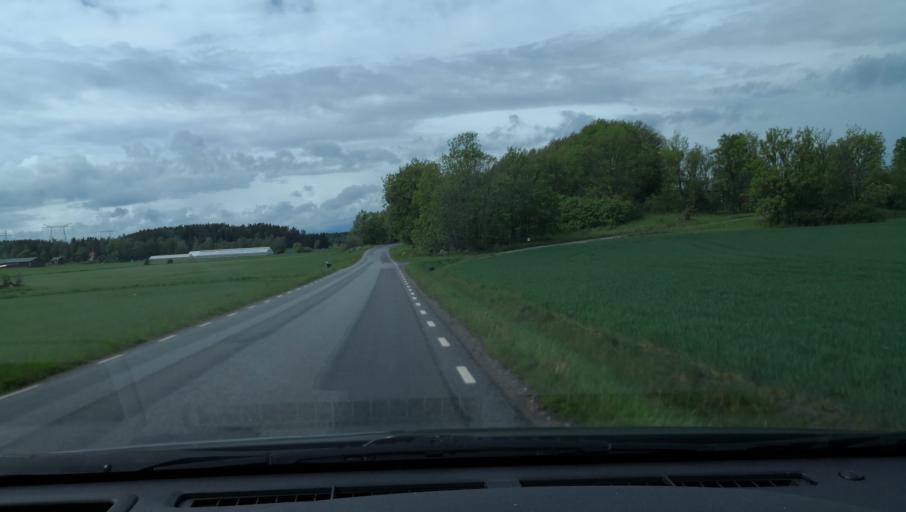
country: SE
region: Uppsala
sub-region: Enkopings Kommun
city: Orsundsbro
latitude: 59.7001
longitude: 17.3638
